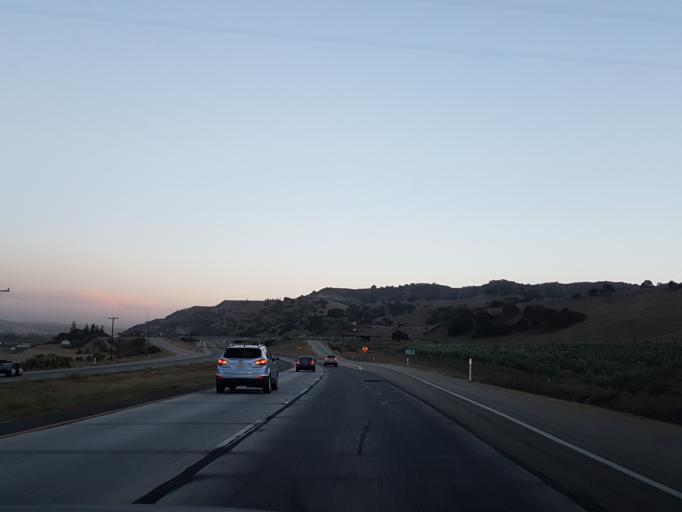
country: US
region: California
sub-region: San Luis Obispo County
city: Lake Nacimiento
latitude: 35.9792
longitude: -120.9018
